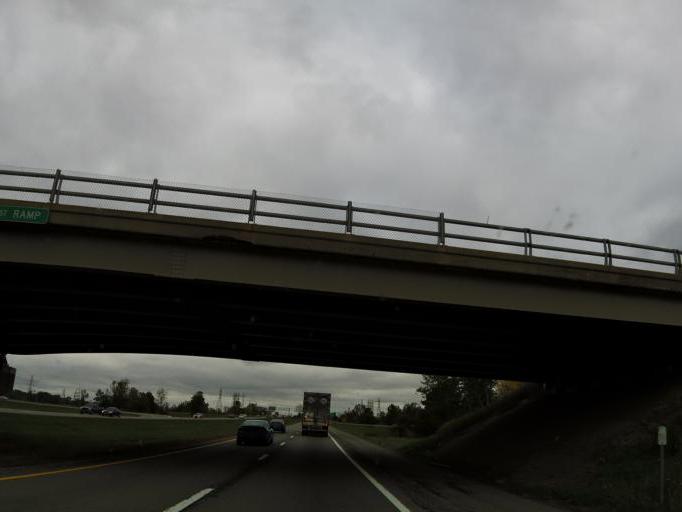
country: US
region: New York
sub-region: Erie County
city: West Seneca
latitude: 42.8480
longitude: -78.7814
